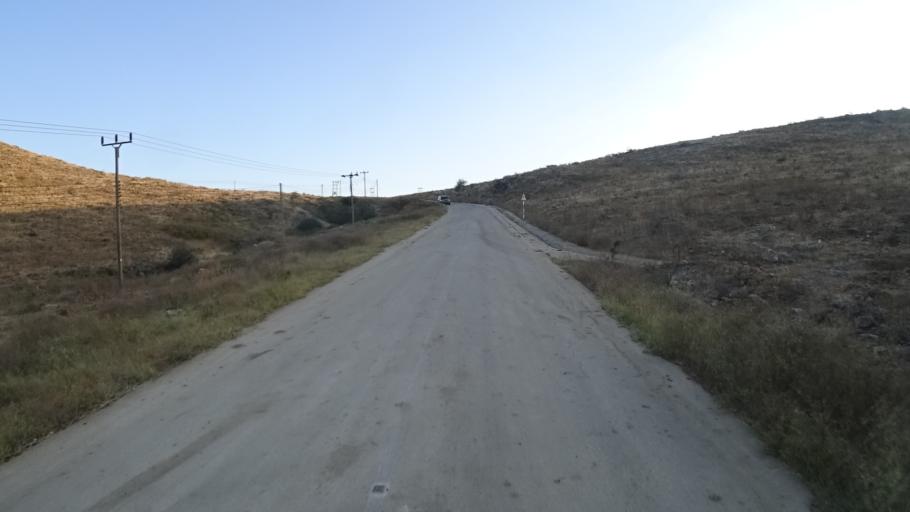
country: OM
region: Zufar
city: Salalah
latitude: 17.1509
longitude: 54.6177
